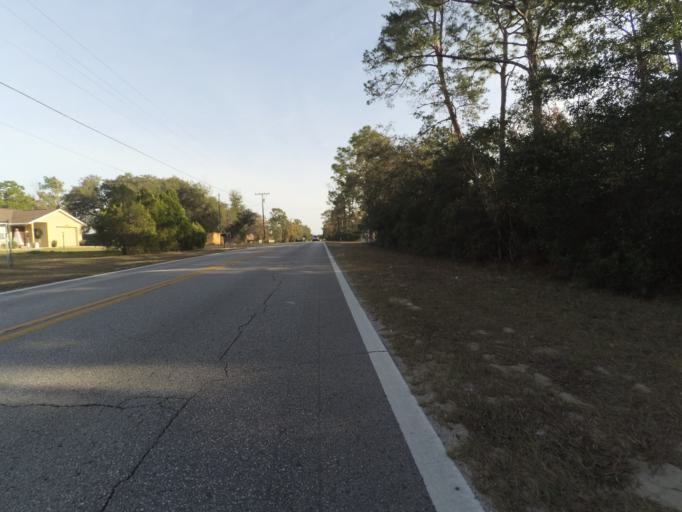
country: US
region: Florida
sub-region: Lake County
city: Umatilla
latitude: 28.9392
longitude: -81.6384
